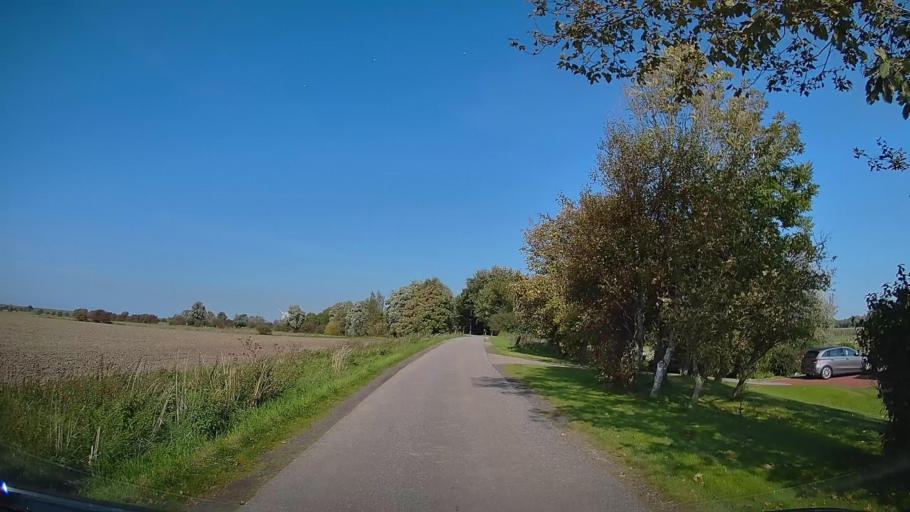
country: DE
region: Lower Saxony
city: Misselwarden
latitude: 53.7038
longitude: 8.5009
